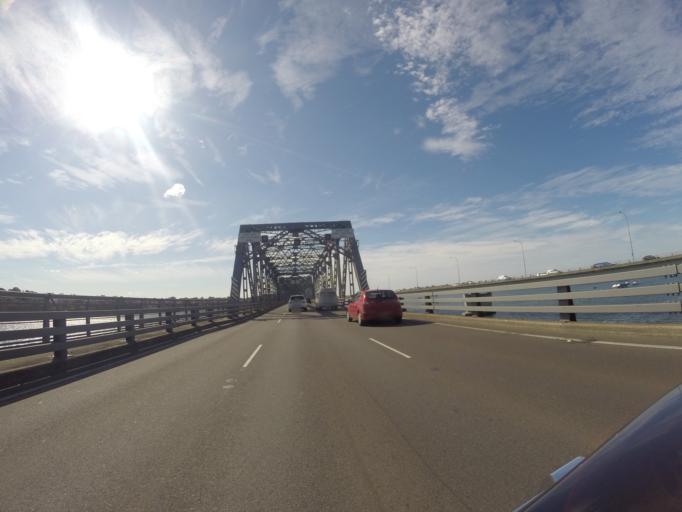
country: AU
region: New South Wales
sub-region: Kogarah
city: Blakehurst
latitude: -34.0039
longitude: 151.1123
